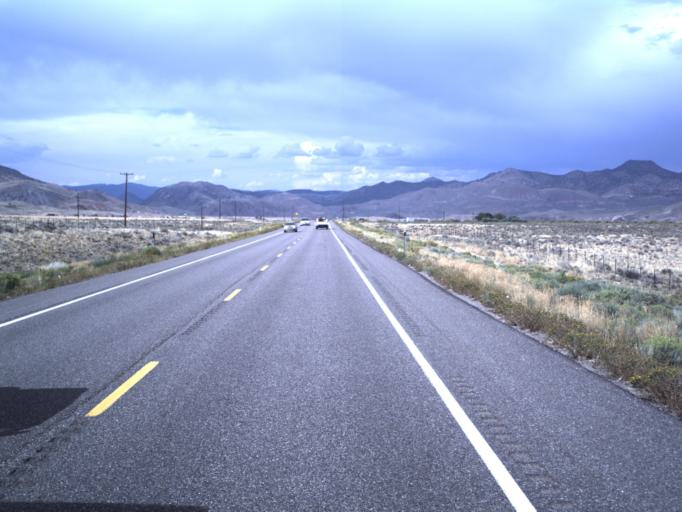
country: US
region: Utah
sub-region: Piute County
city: Junction
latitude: 38.4240
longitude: -112.2316
